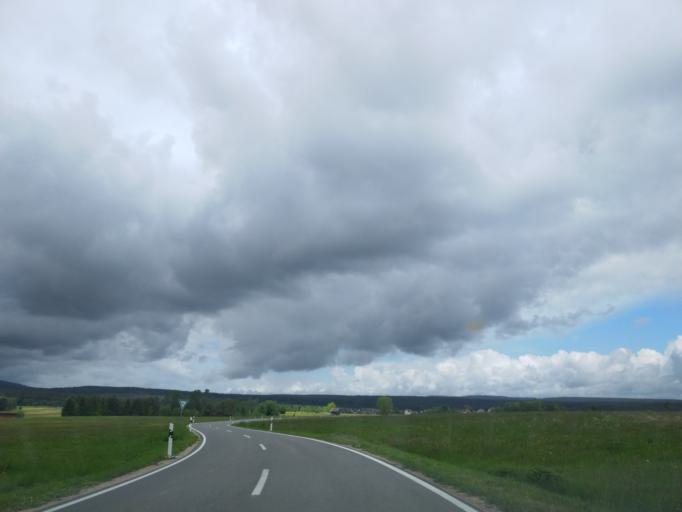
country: DE
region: Baden-Wuerttemberg
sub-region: Freiburg Region
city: Loffingen
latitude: 47.8810
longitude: 8.3087
